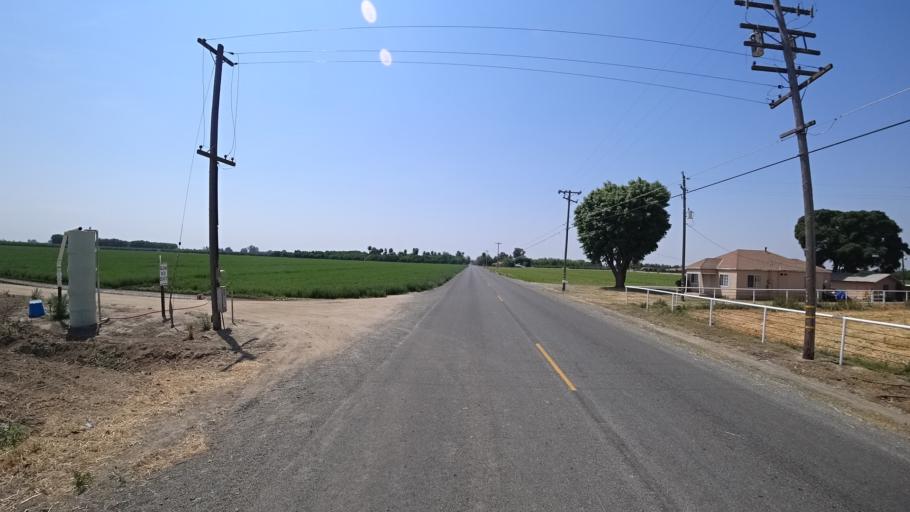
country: US
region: California
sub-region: Kings County
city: Lemoore
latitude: 36.3243
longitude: -119.7628
